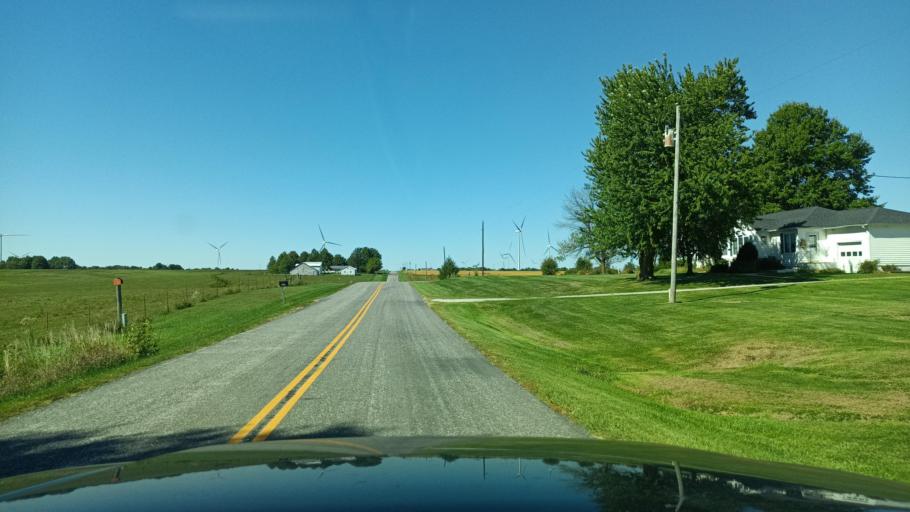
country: US
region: Missouri
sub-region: Adair County
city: Kirksville
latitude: 40.3307
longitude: -92.4649
